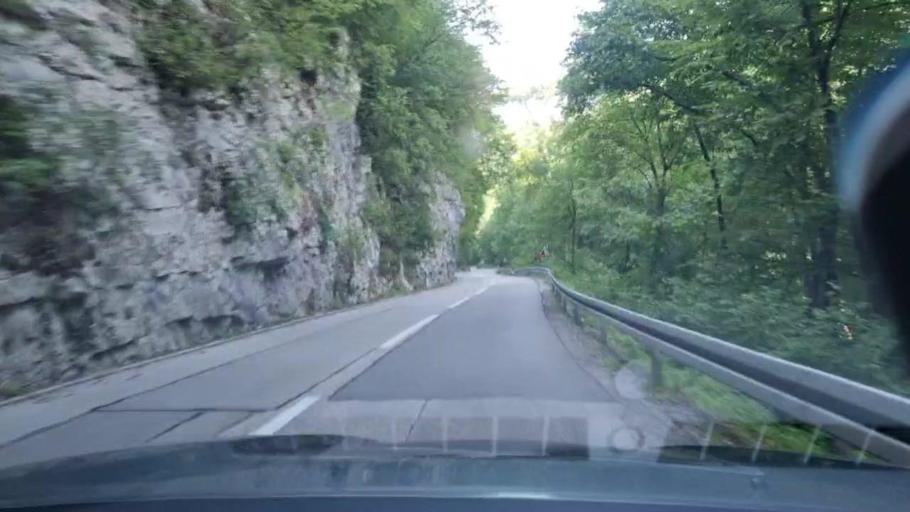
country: BA
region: Federation of Bosnia and Herzegovina
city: Bosanska Krupa
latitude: 44.8676
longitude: 16.0883
